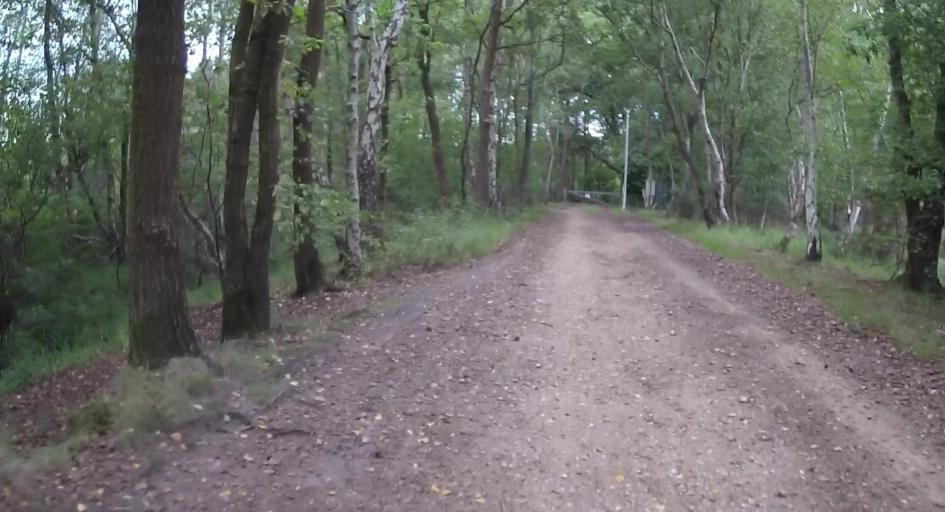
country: GB
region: England
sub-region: Surrey
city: Windlesham
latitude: 51.3390
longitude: -0.6625
